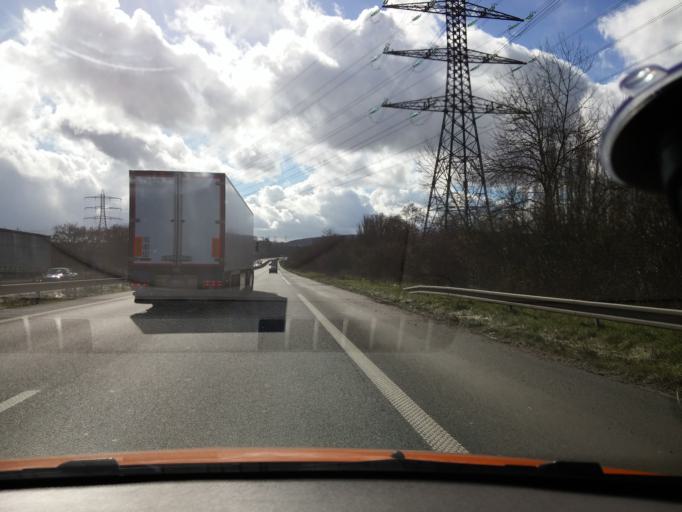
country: FR
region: Ile-de-France
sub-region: Departement de l'Essonne
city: Palaiseau
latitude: 48.7115
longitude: 2.2521
